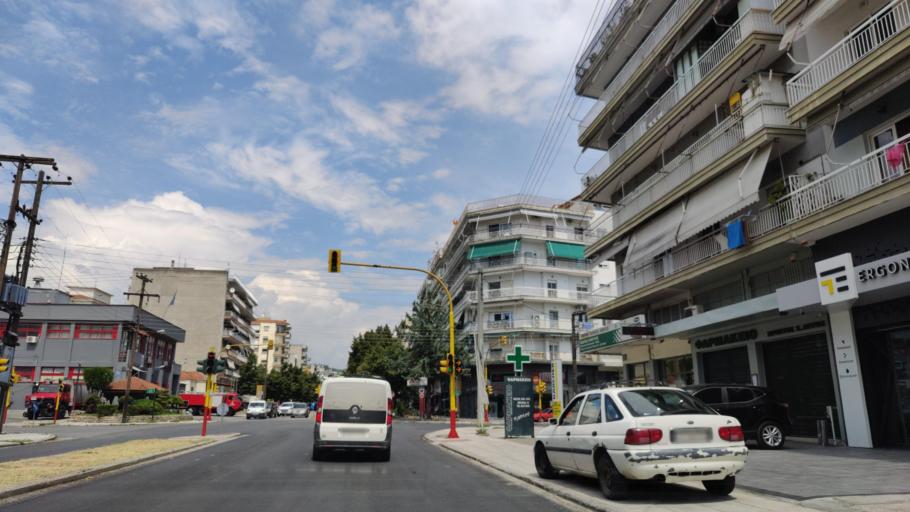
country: GR
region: Central Macedonia
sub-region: Nomos Serron
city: Serres
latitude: 41.0820
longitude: 23.5424
